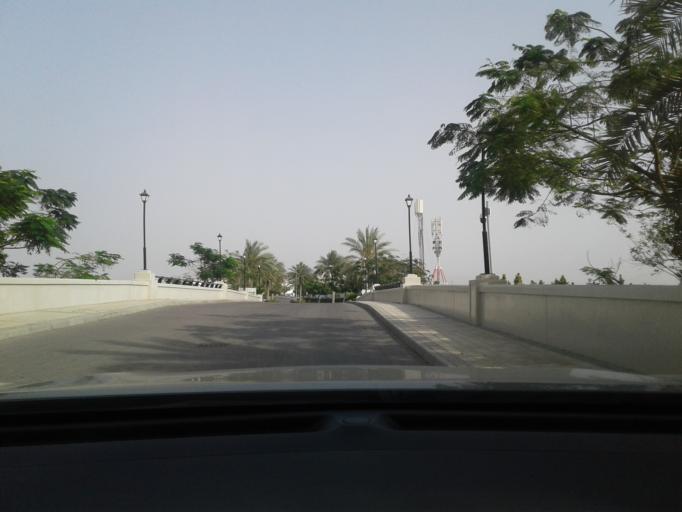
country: OM
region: Muhafazat Masqat
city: As Sib al Jadidah
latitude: 23.6237
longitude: 58.2734
